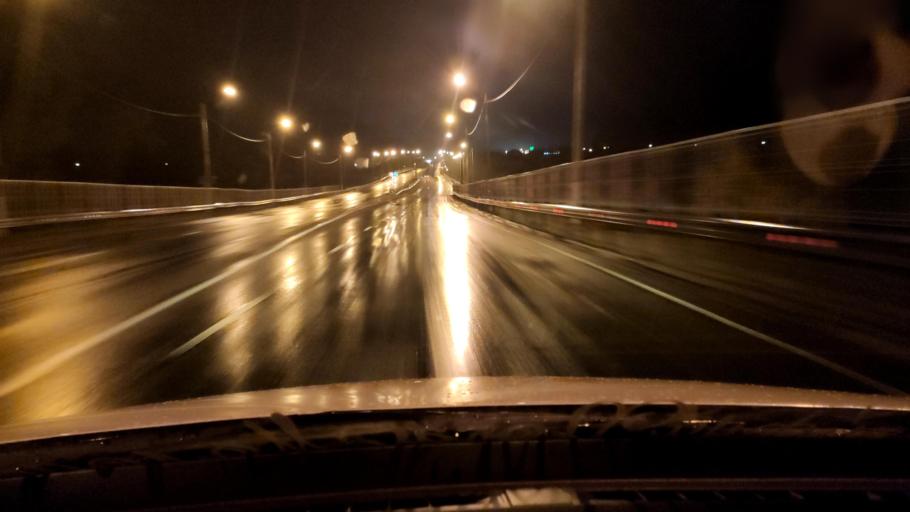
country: RU
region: Voronezj
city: Devitsa
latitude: 51.6354
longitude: 38.9400
